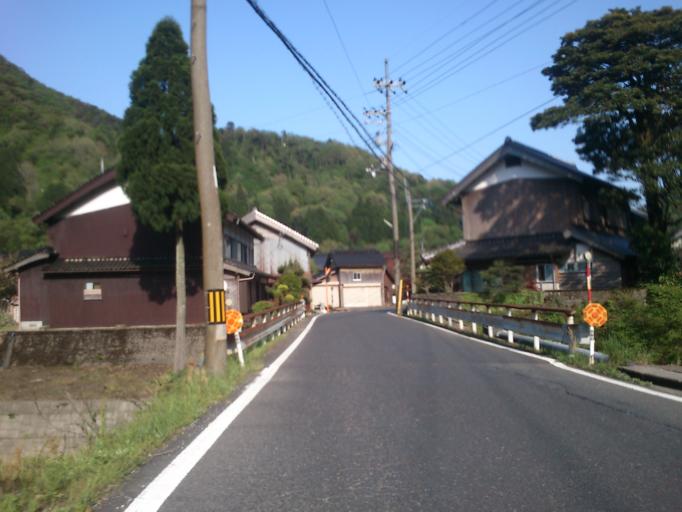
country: JP
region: Kyoto
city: Miyazu
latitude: 35.7116
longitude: 135.2375
